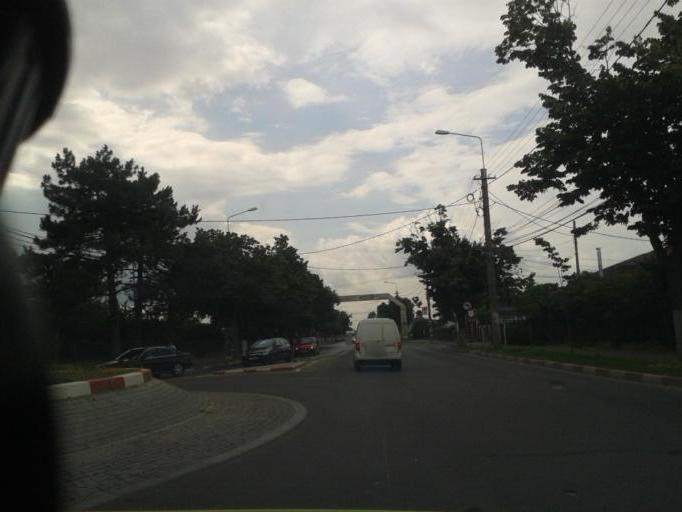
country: RO
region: Prahova
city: Ploiesti
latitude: 44.9565
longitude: 25.9895
